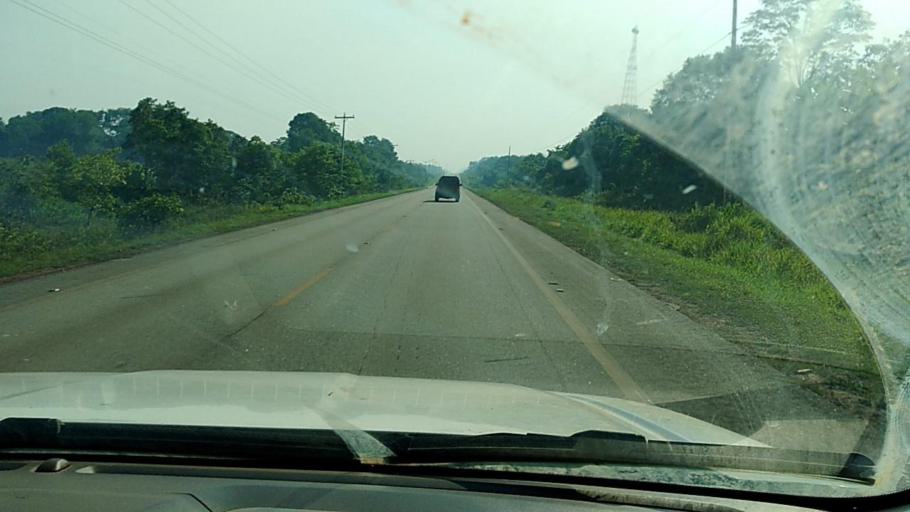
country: BR
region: Amazonas
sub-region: Humaita
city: Humaita
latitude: -8.0289
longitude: -63.4508
